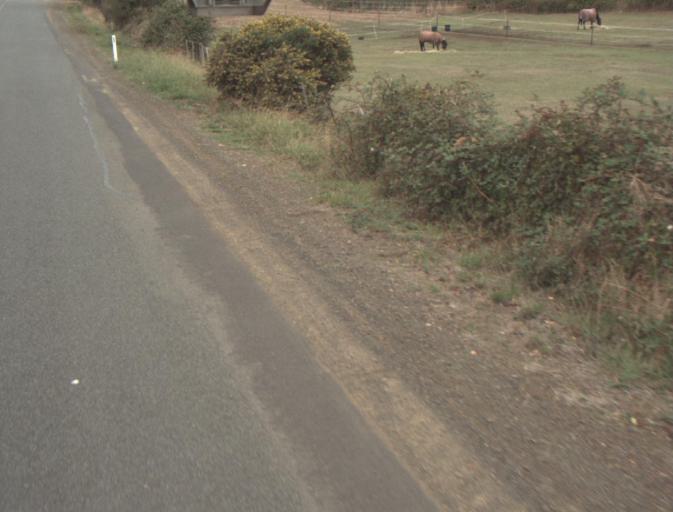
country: AU
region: Tasmania
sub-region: Launceston
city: Summerhill
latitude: -41.4930
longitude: 147.1767
